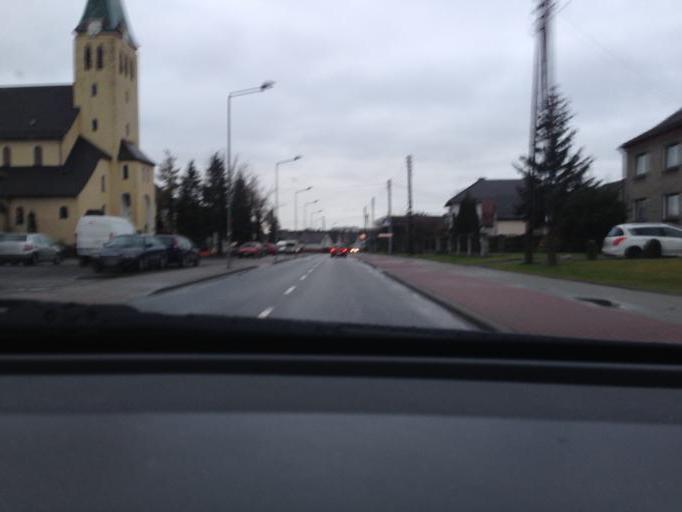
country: PL
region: Opole Voivodeship
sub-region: Powiat opolski
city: Opole
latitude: 50.6818
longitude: 17.9573
